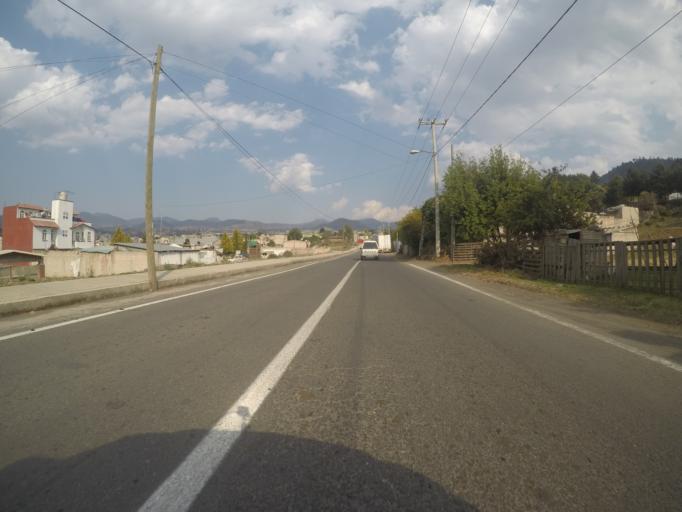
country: MX
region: Mexico
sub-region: Xalatlaco
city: Techichili
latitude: 19.1754
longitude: -99.4251
